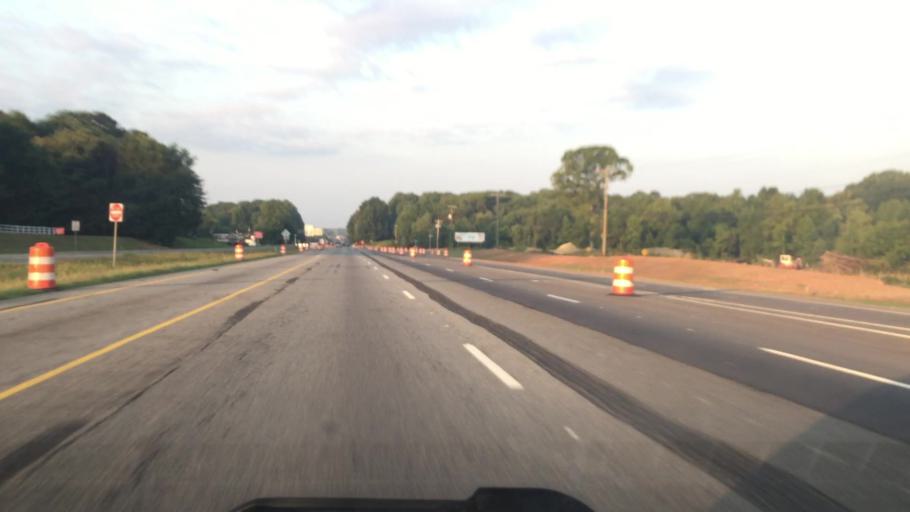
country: US
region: North Carolina
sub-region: Guilford County
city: Greensboro
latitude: 36.1368
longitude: -79.7399
